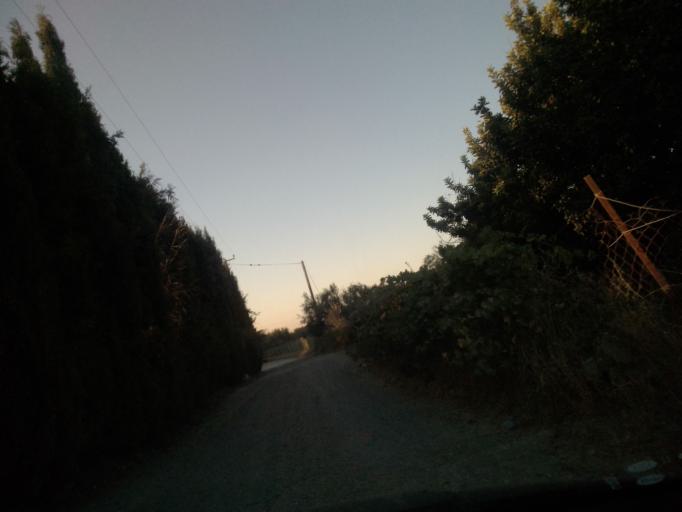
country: CY
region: Limassol
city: Ypsonas
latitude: 34.6711
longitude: 32.9649
